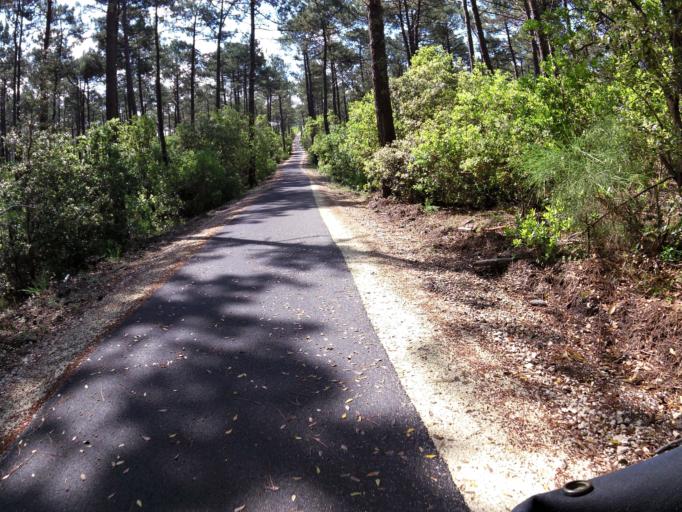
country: FR
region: Aquitaine
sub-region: Departement de la Gironde
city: Lacanau
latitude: 45.0360
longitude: -1.1829
